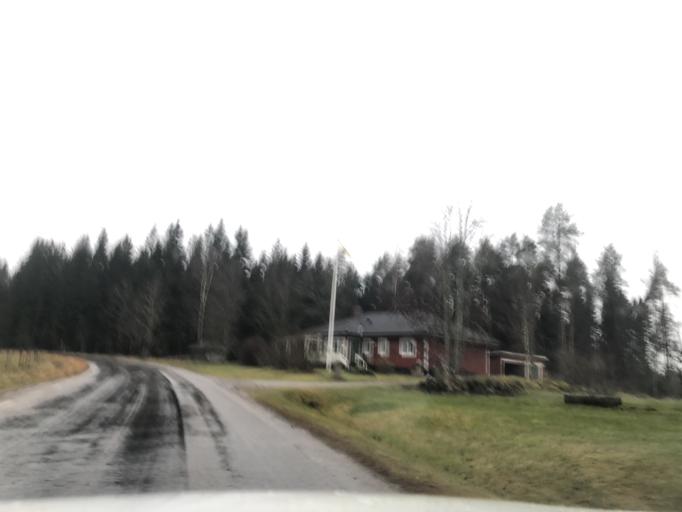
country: SE
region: Vaestra Goetaland
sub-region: Ulricehamns Kommun
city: Ulricehamn
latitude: 57.8436
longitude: 13.5400
